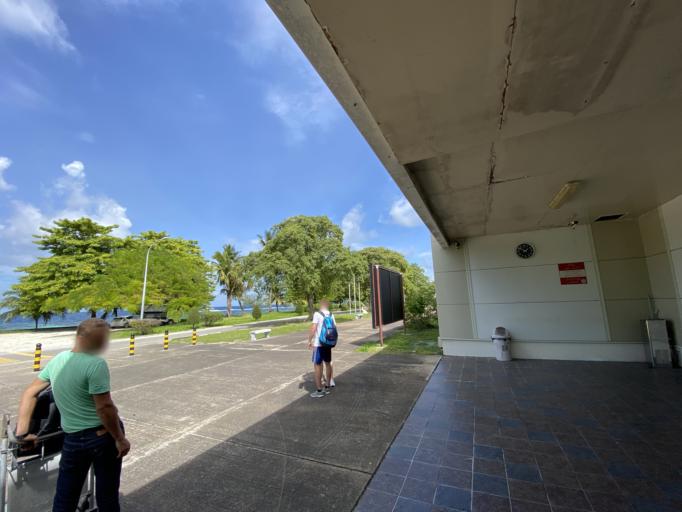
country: MV
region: South Province
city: Hithadhoo
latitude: -0.6899
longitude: 73.1559
